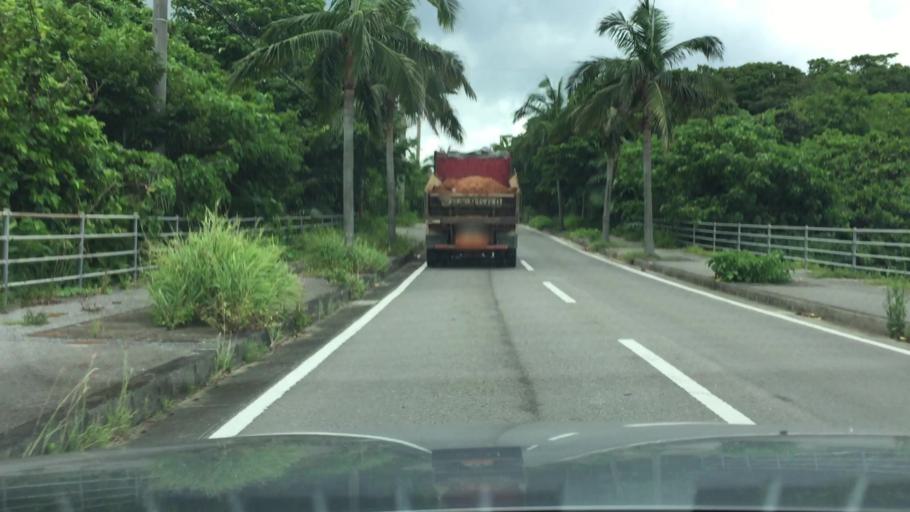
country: JP
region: Okinawa
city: Ishigaki
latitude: 24.4538
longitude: 124.1991
